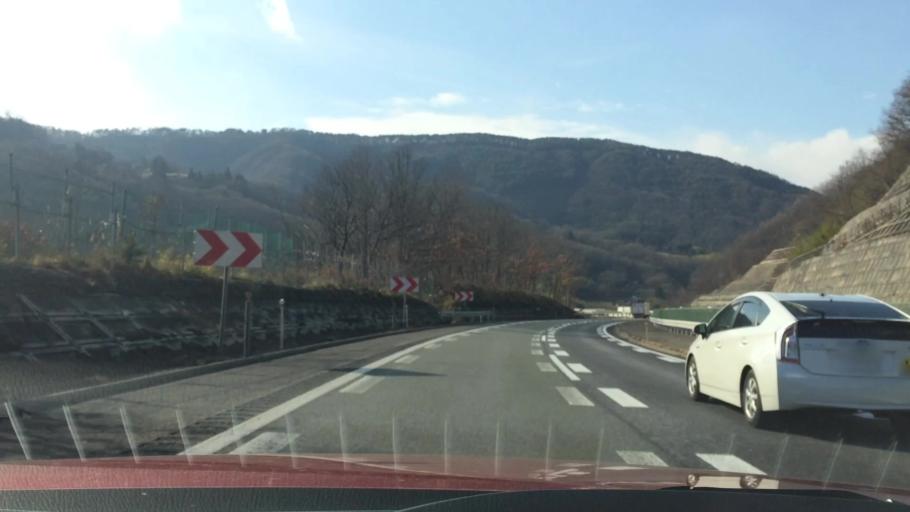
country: JP
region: Nagano
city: Toyoshina
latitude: 36.3446
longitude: 137.9597
